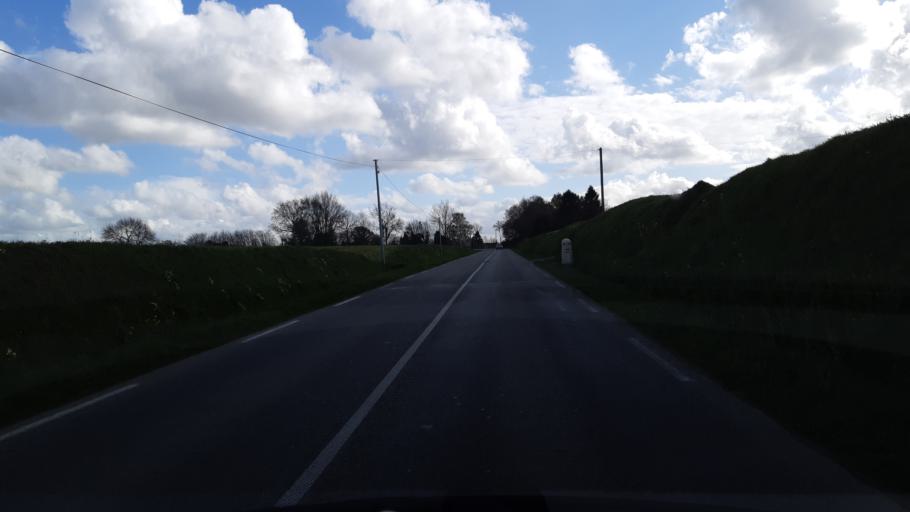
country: FR
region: Lower Normandy
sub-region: Departement de la Manche
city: Agneaux
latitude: 49.0606
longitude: -1.1331
